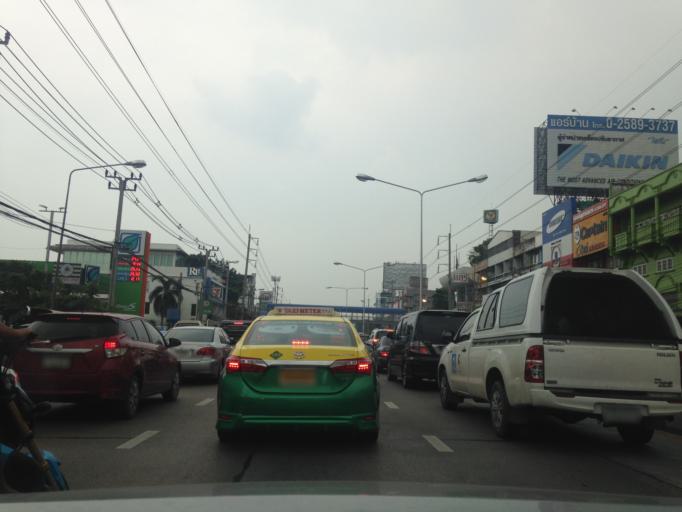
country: TH
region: Nonthaburi
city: Mueang Nonthaburi
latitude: 13.8583
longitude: 100.5293
